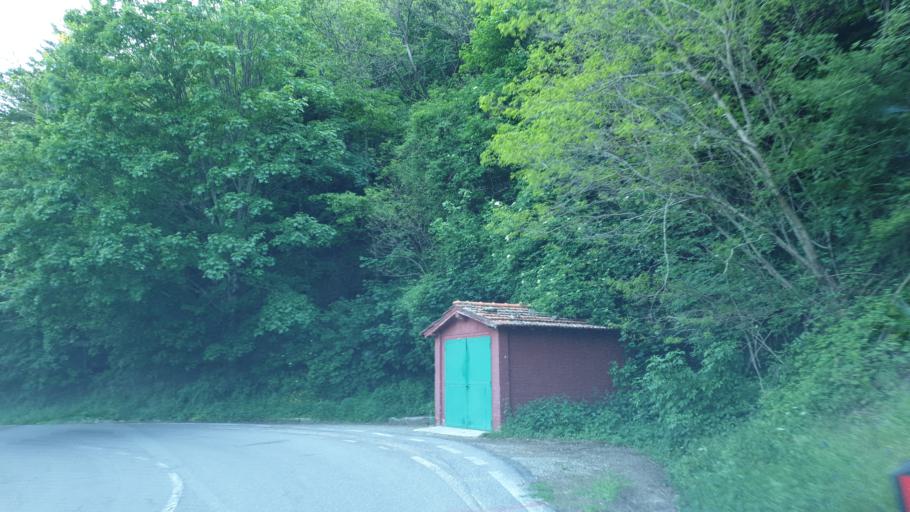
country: IT
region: Tuscany
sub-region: Province of Arezzo
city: Soci
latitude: 43.7788
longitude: 11.8693
